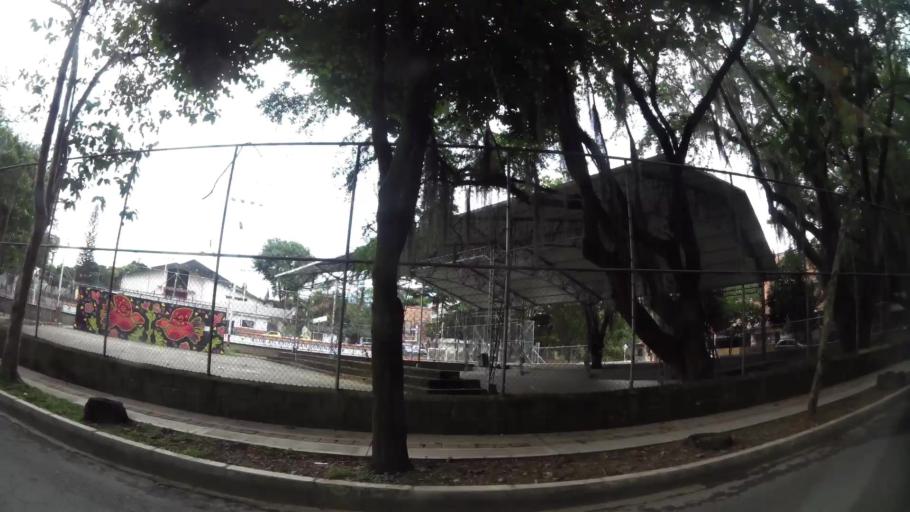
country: CO
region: Antioquia
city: Envigado
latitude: 6.1640
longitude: -75.5946
